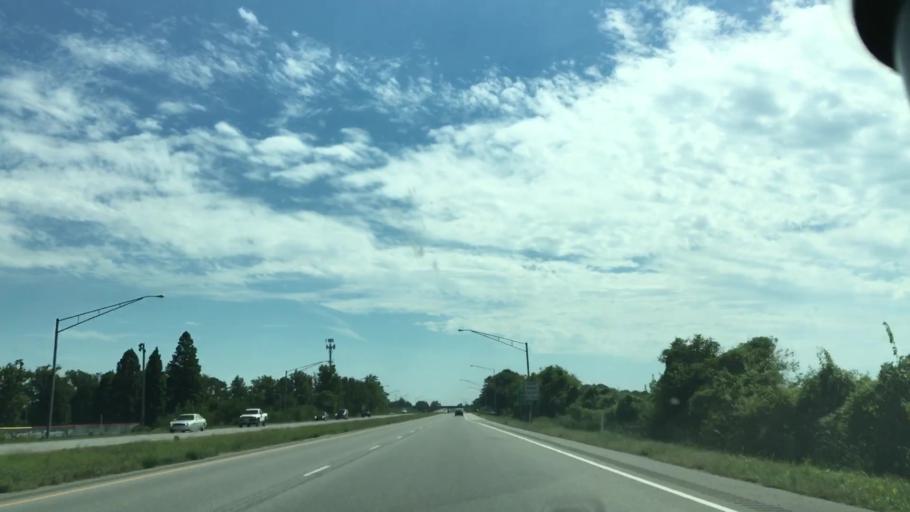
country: US
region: Kentucky
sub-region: Daviess County
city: Owensboro
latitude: 37.7621
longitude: -87.1625
